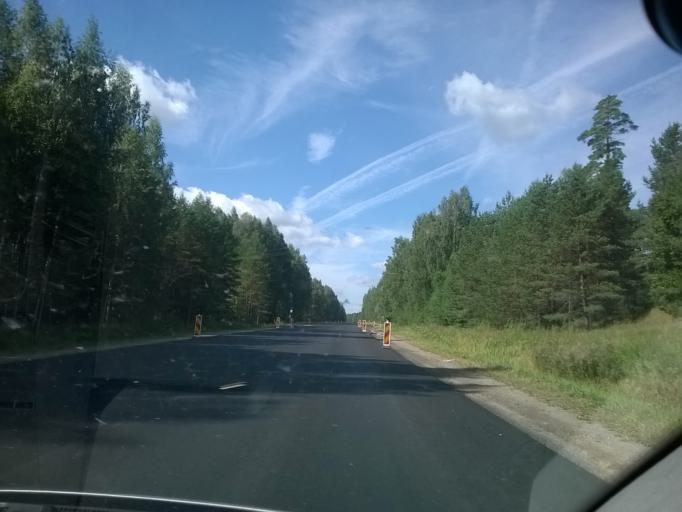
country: EE
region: Vorumaa
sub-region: Voru linn
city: Voru
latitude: 57.8170
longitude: 26.9925
